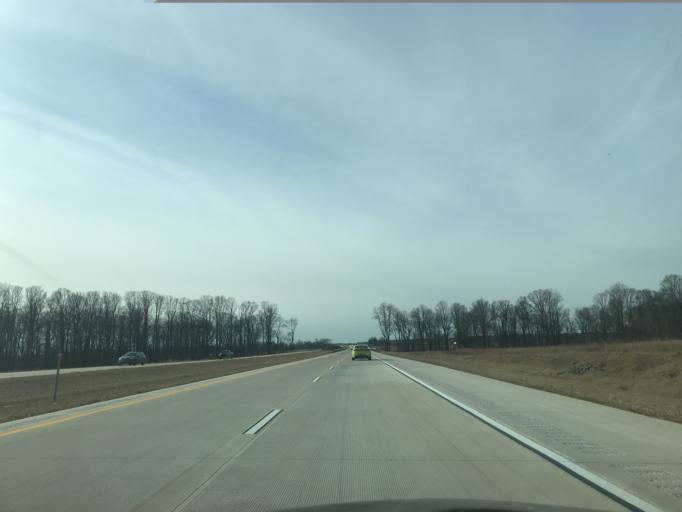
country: US
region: Delaware
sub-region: New Castle County
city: Middletown
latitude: 39.4983
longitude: -75.6987
